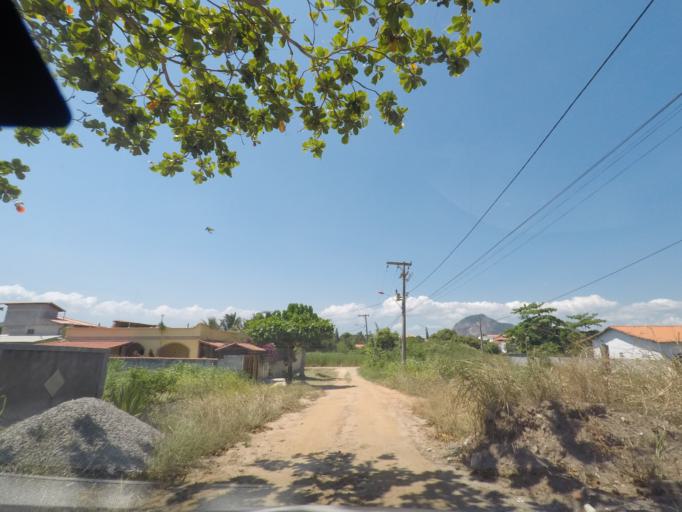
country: BR
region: Rio de Janeiro
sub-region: Marica
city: Marica
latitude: -22.9724
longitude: -42.9316
